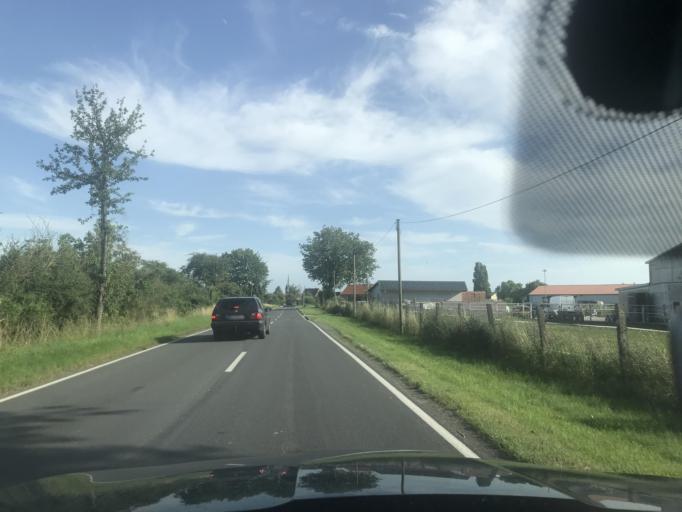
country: DE
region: Saxony-Anhalt
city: Ditfurt
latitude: 51.8375
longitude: 11.1980
